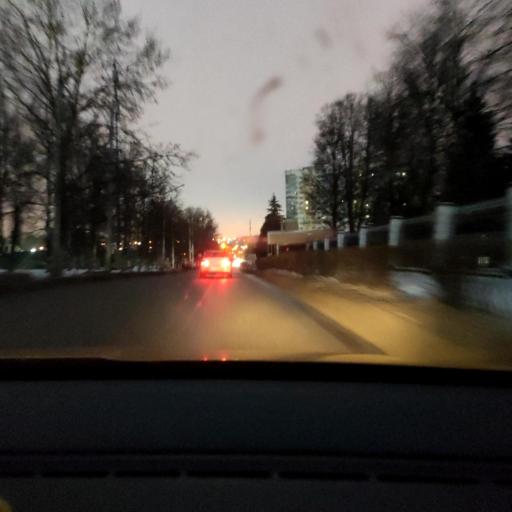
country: RU
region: Moskovskaya
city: Mosrentgen
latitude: 55.6156
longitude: 37.4667
